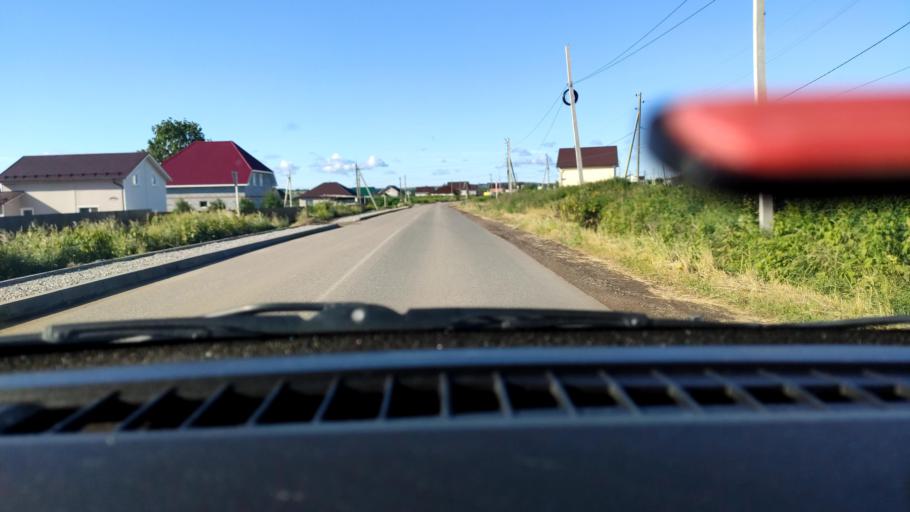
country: RU
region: Perm
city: Kultayevo
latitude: 57.8657
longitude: 55.9157
